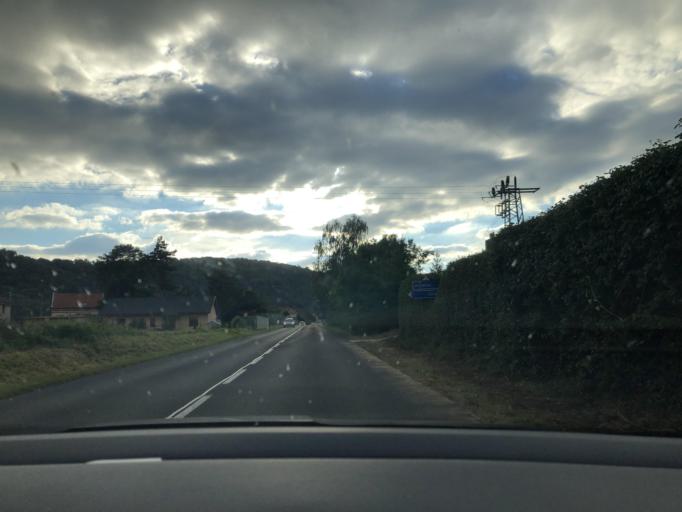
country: CZ
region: Ustecky
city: Velke Brezno
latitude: 50.6651
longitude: 14.1058
